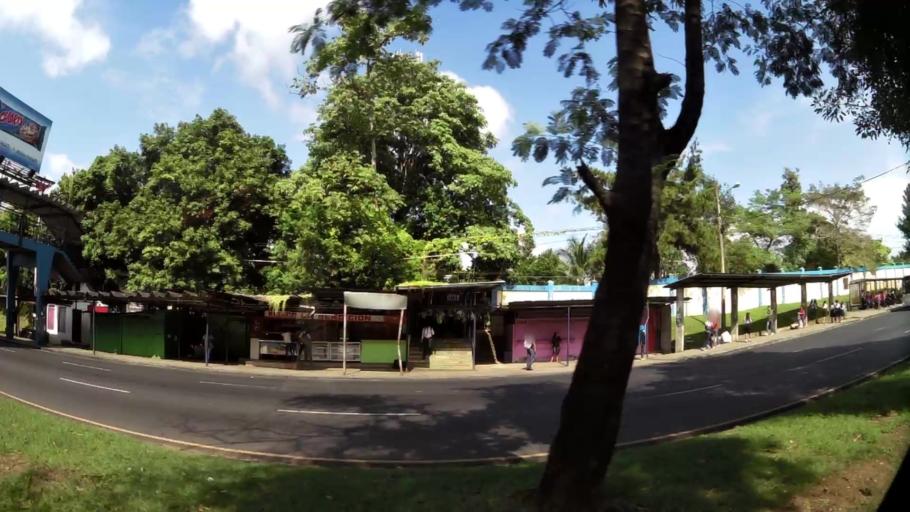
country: PA
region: Panama
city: Panama
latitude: 8.9848
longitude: -79.5351
